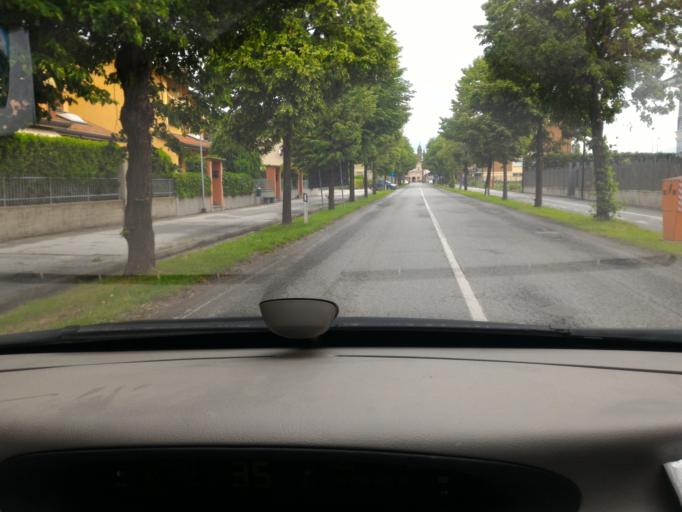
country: IT
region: Piedmont
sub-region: Provincia di Cuneo
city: Genola
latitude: 44.5907
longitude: 7.6608
